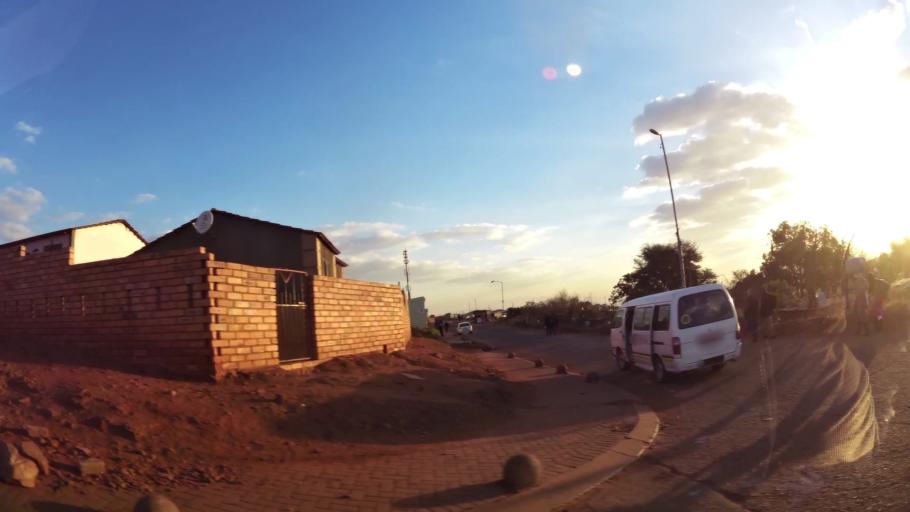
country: ZA
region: Gauteng
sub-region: West Rand District Municipality
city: Krugersdorp
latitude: -26.0718
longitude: 27.7537
